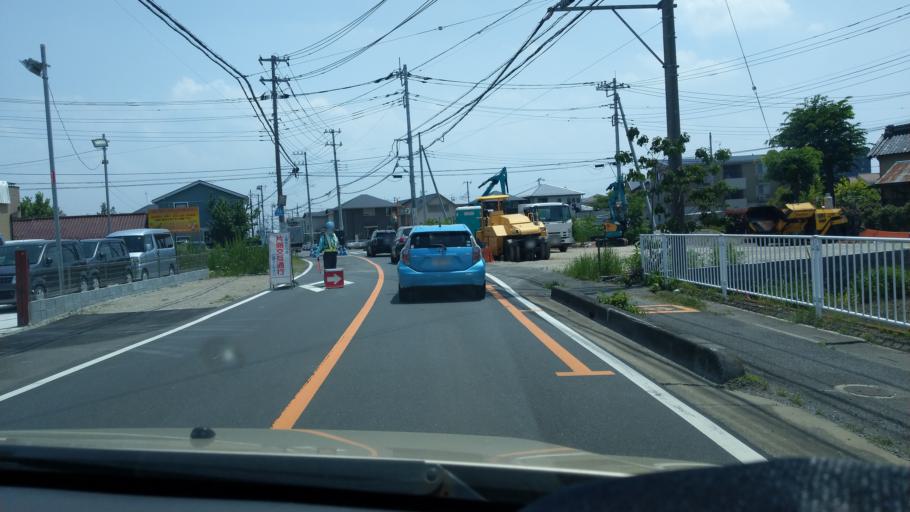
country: JP
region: Saitama
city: Iwatsuki
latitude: 35.9090
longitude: 139.7274
